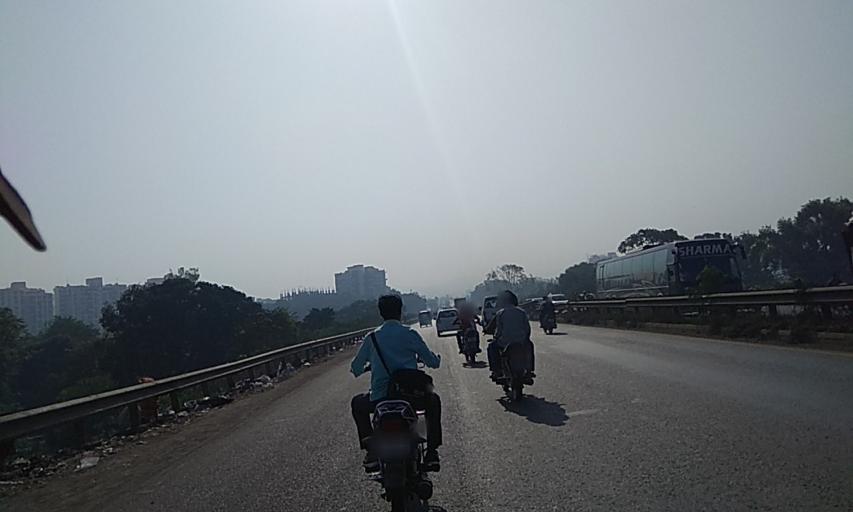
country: IN
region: Maharashtra
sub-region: Pune Division
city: Kharakvasla
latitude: 18.4769
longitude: 73.8074
